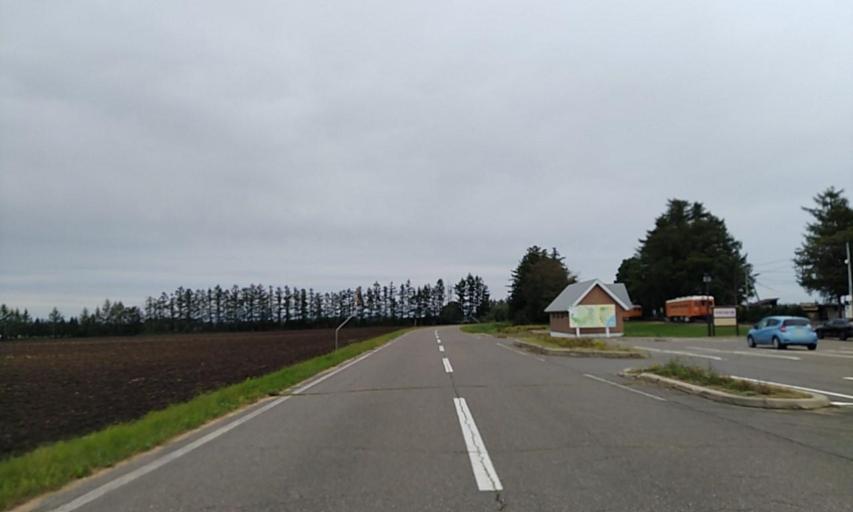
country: JP
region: Hokkaido
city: Obihiro
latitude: 42.7442
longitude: 143.1612
